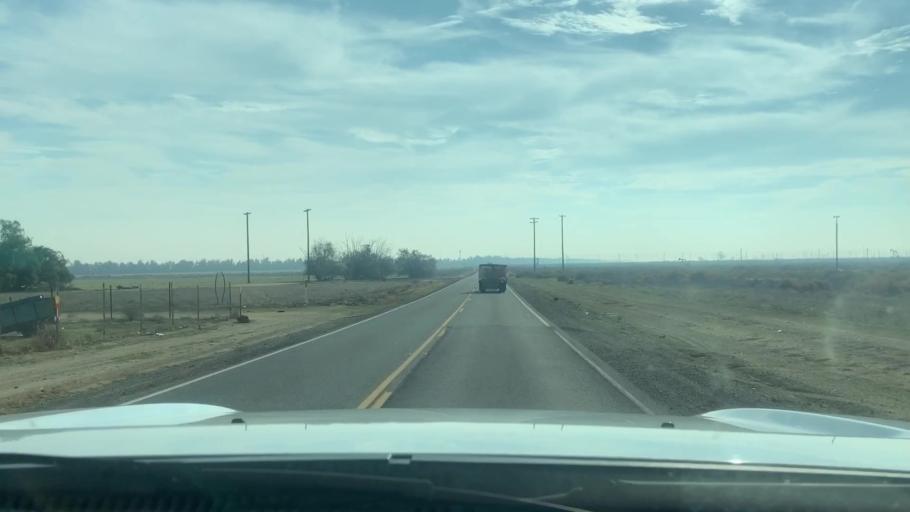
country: US
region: California
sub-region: Kern County
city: Lost Hills
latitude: 35.5365
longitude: -119.7712
